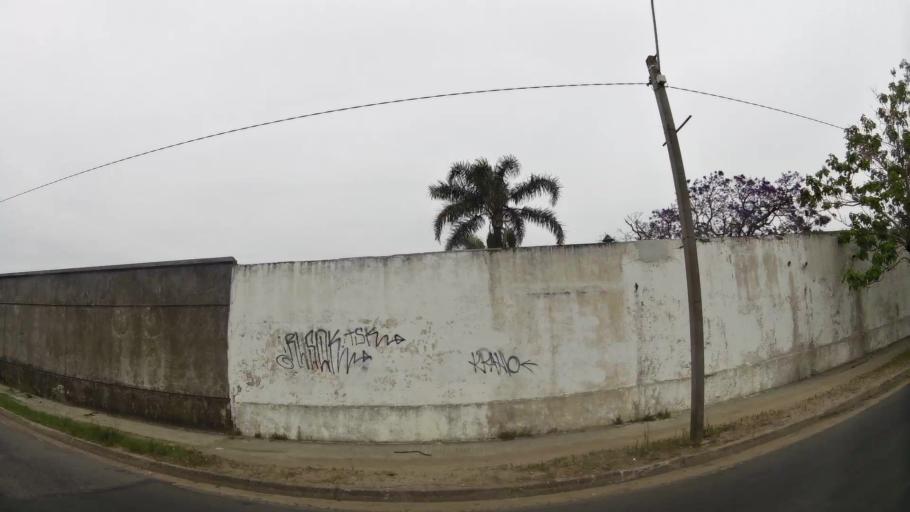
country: UY
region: Canelones
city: La Paz
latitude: -34.7543
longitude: -56.2278
